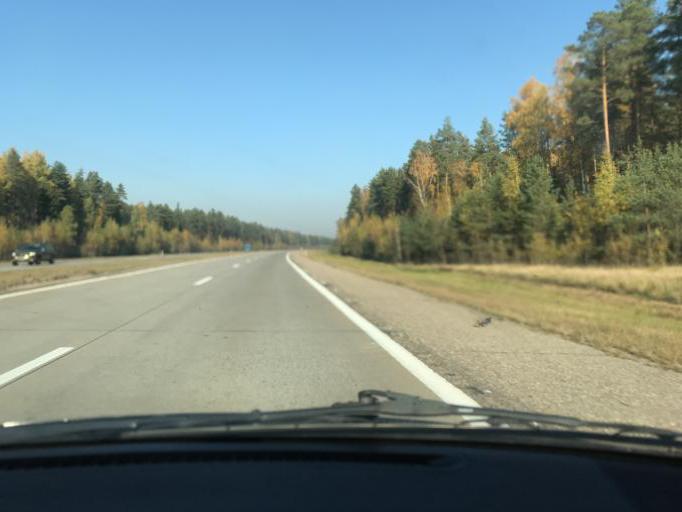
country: BY
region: Minsk
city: Uzda
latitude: 53.3979
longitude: 27.4815
